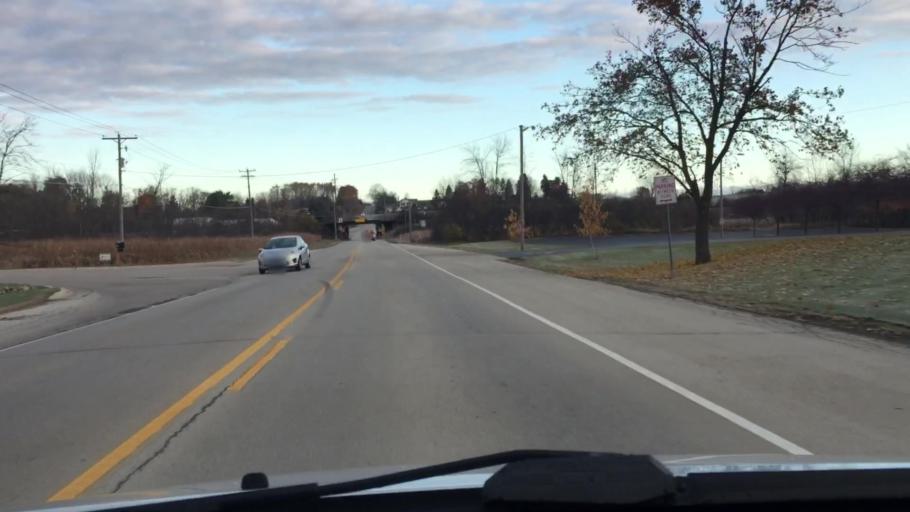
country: US
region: Wisconsin
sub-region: Waukesha County
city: Okauchee Lake
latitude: 43.1750
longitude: -88.4590
